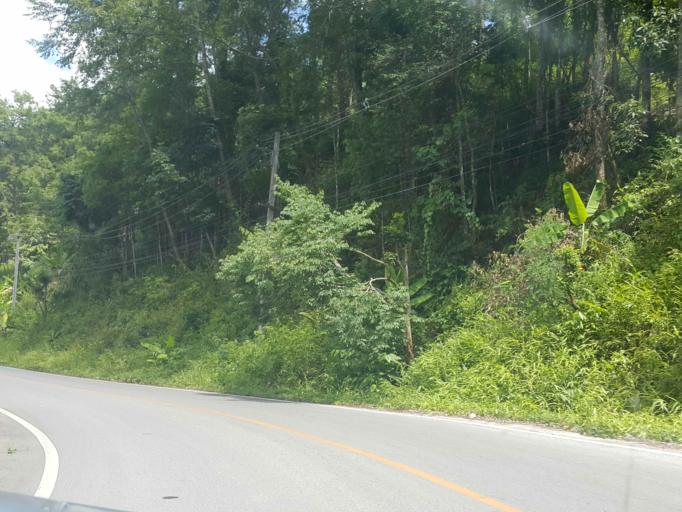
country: TH
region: Chiang Mai
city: Samoeng
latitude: 18.8768
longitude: 98.7893
